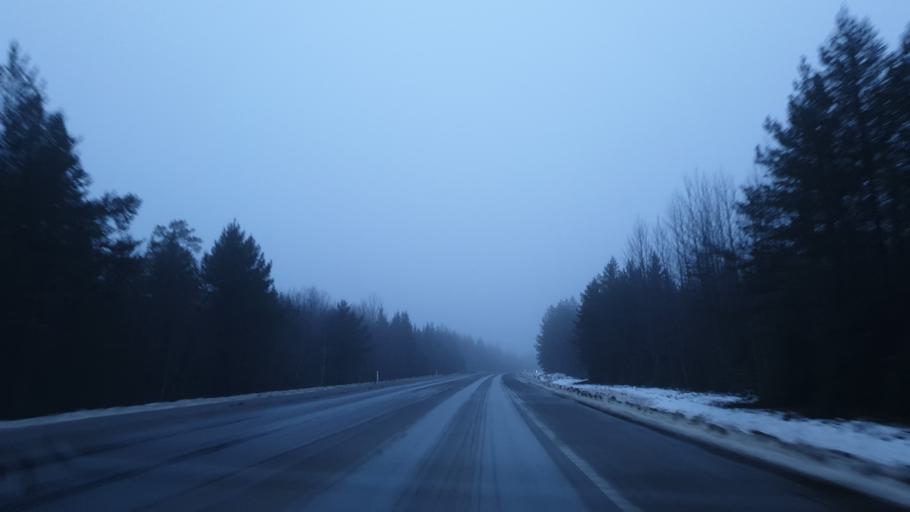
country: SE
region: Vaesterbotten
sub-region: Umea Kommun
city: Holmsund
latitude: 63.7595
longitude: 20.3473
